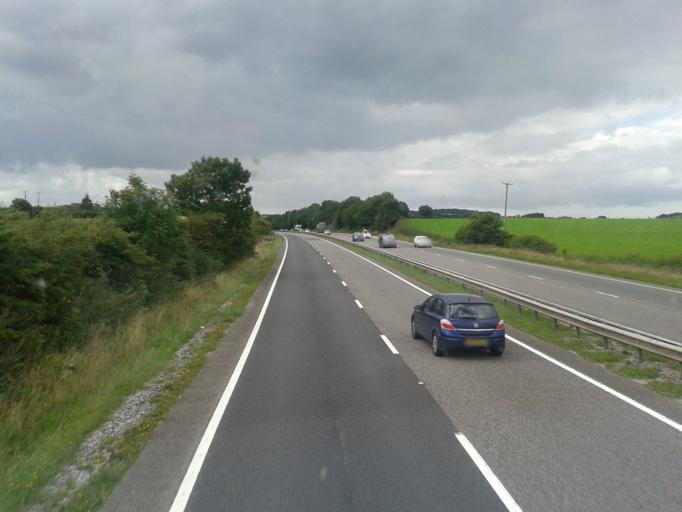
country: GB
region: England
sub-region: Devon
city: Crediton
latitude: 50.7279
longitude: -3.6687
